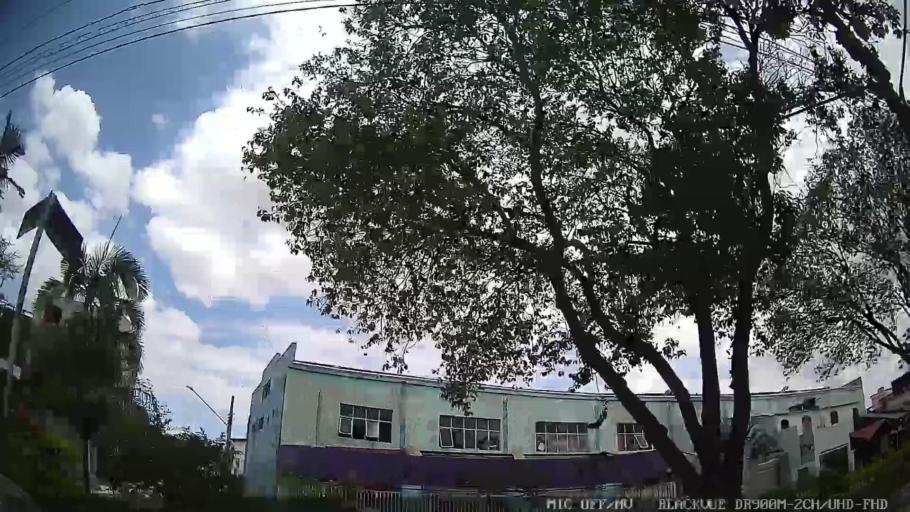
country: BR
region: Sao Paulo
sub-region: Guarulhos
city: Guarulhos
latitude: -23.5144
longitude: -46.5398
